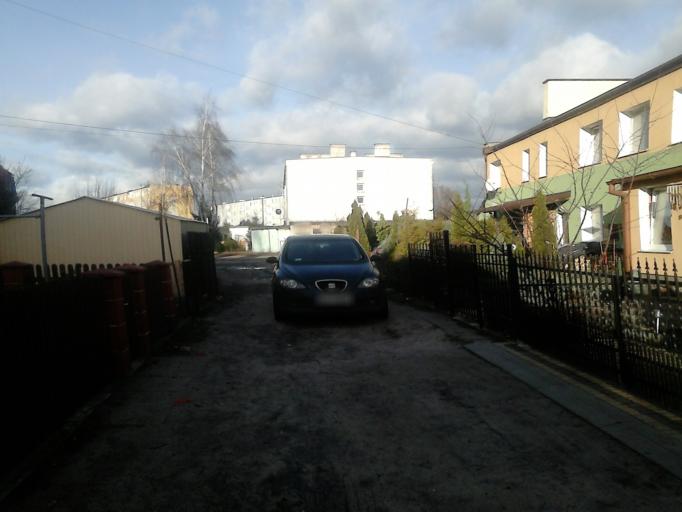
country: PL
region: Pomeranian Voivodeship
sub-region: Gdansk
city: Gdansk
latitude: 54.3634
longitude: 18.7098
